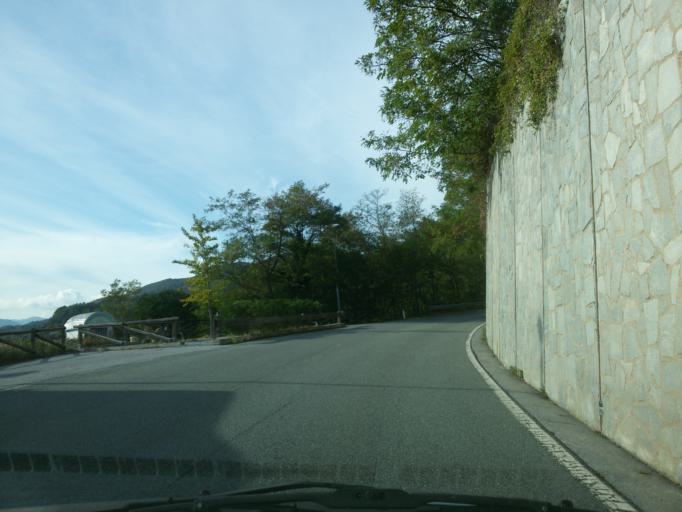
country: IT
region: Liguria
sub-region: Provincia di Genova
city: Piccarello
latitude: 44.4876
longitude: 8.9753
